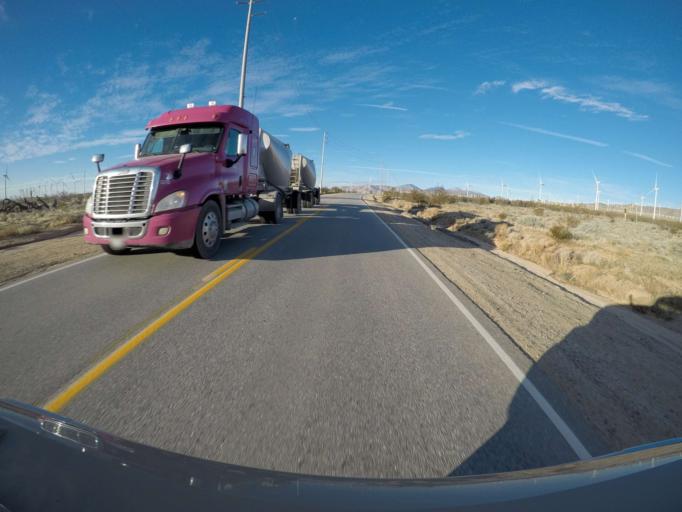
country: US
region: California
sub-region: Kern County
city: Mojave
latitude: 35.0414
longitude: -118.2351
